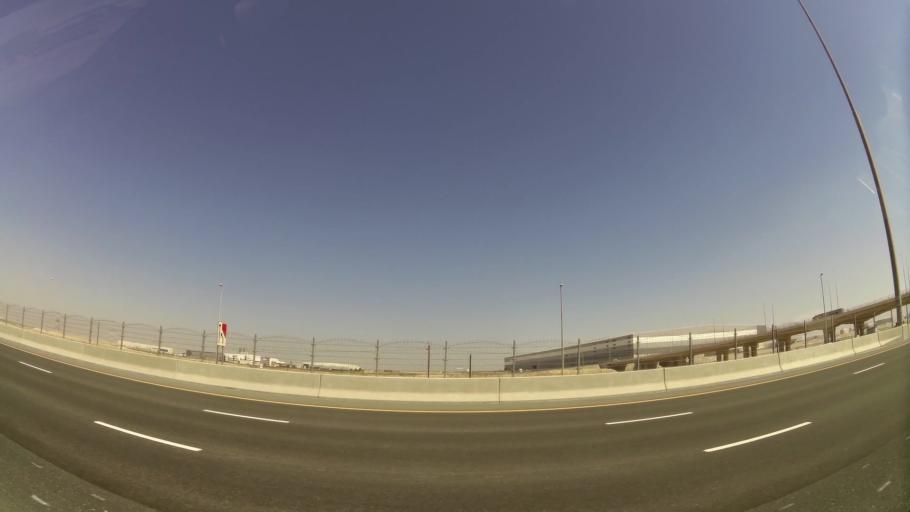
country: AE
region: Dubai
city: Dubai
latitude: 24.9248
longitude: 55.1104
